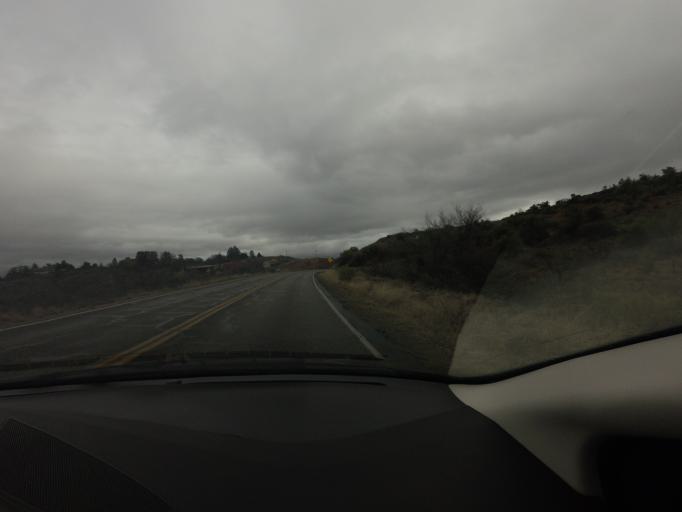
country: US
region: Arizona
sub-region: Yavapai County
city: Clarkdale
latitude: 34.7631
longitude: -112.0412
